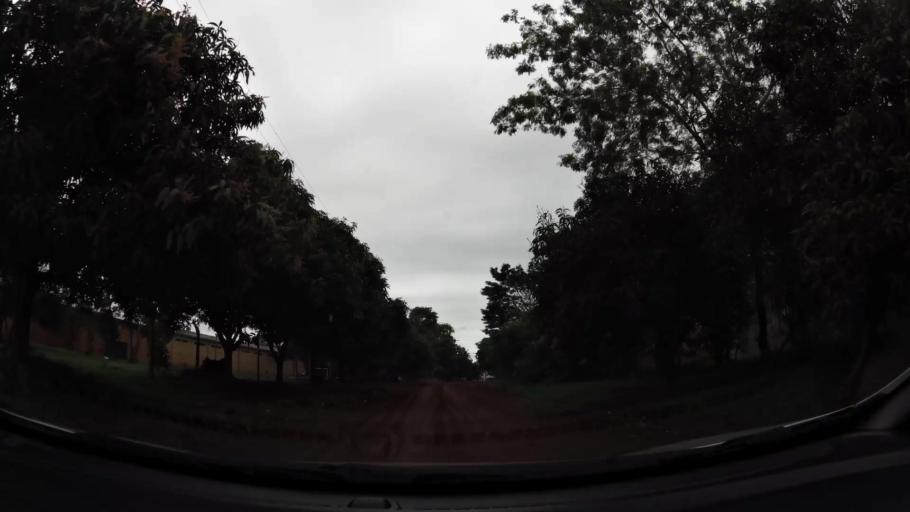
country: PY
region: Alto Parana
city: Ciudad del Este
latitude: -25.4376
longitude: -54.6386
